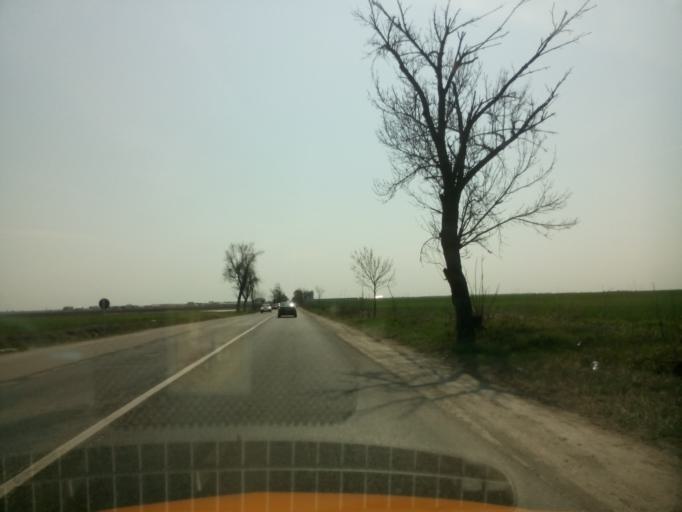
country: RO
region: Ilfov
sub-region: Comuna Glina
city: Glina
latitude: 44.3485
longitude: 26.2204
